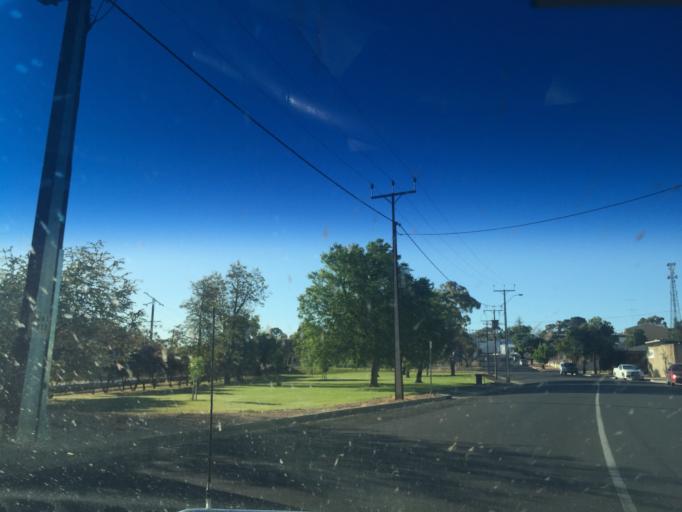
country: AU
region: South Australia
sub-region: Berri and Barmera
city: Berri
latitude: -34.2882
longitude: 140.6007
